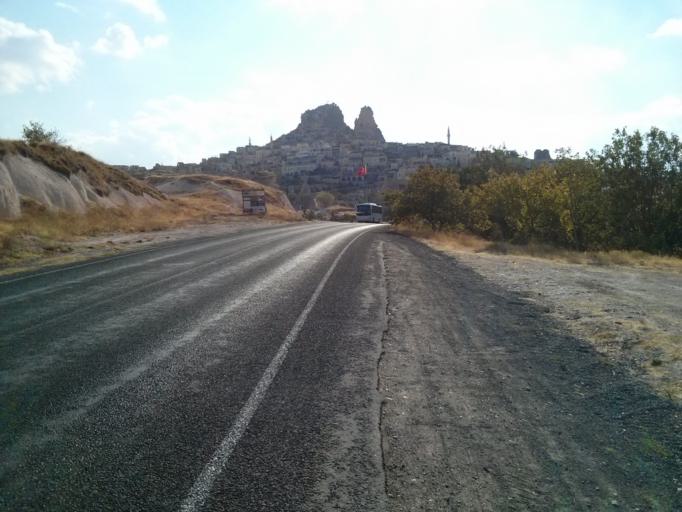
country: TR
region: Nevsehir
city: Goereme
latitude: 38.6405
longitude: 34.8178
